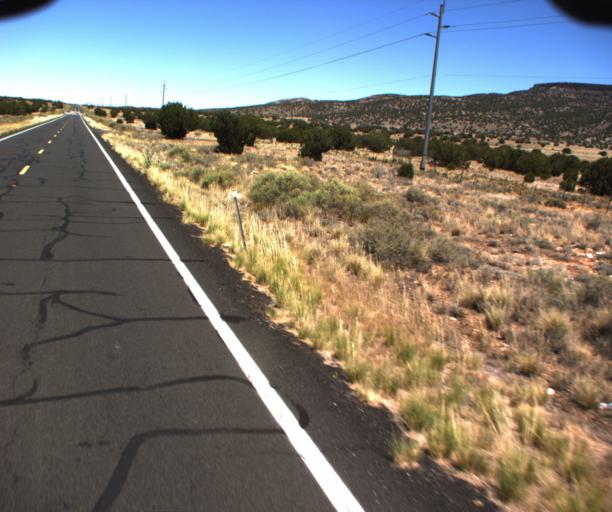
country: US
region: Arizona
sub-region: Coconino County
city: LeChee
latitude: 34.8461
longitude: -110.9329
